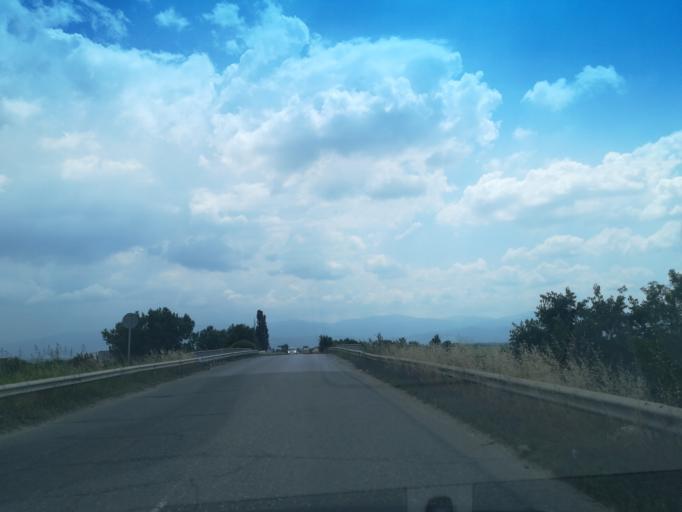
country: BG
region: Plovdiv
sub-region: Obshtina Plovdiv
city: Plovdiv
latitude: 42.1912
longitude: 24.6765
